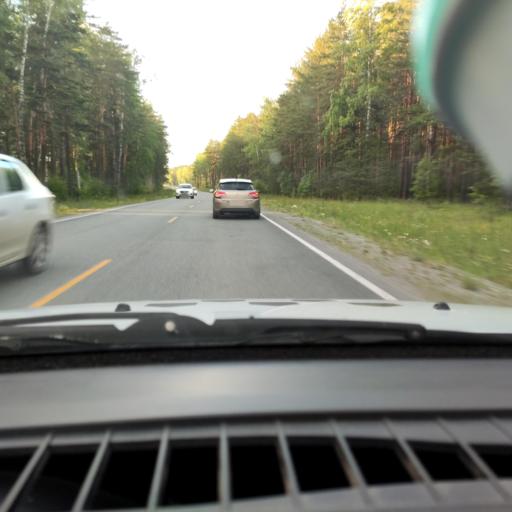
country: RU
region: Chelyabinsk
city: Turgoyak
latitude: 55.2808
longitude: 60.1973
